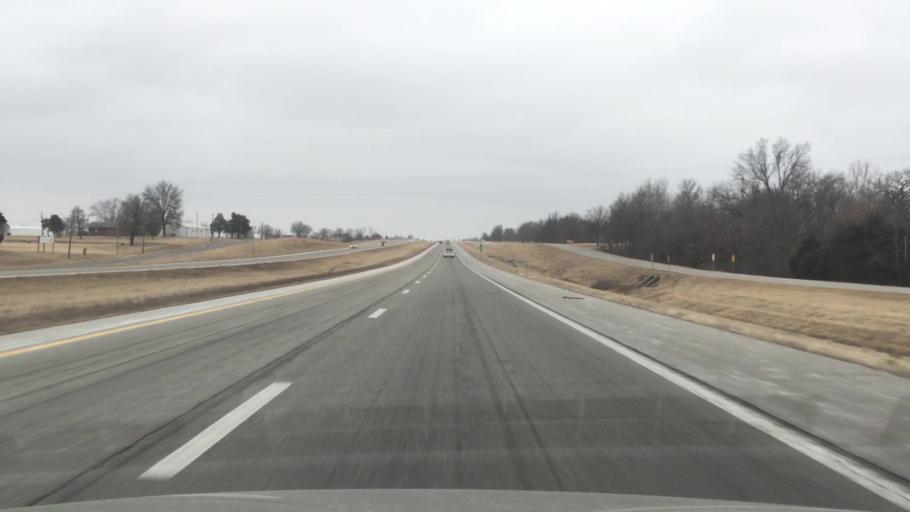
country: US
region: Missouri
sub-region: Cass County
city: Harrisonville
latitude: 38.5980
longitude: -94.3498
